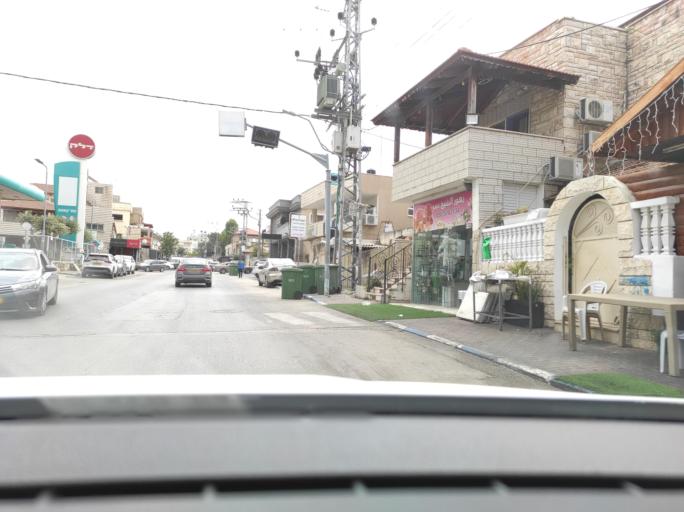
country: IL
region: Central District
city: Kafr Qasim
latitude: 32.1169
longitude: 34.9700
